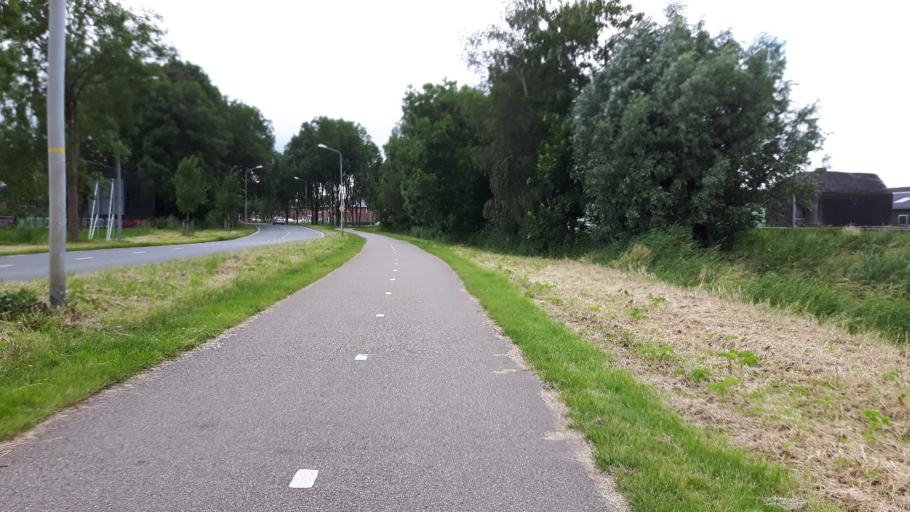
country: NL
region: Utrecht
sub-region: Stichtse Vecht
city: Vreeland
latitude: 52.2508
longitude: 5.0520
